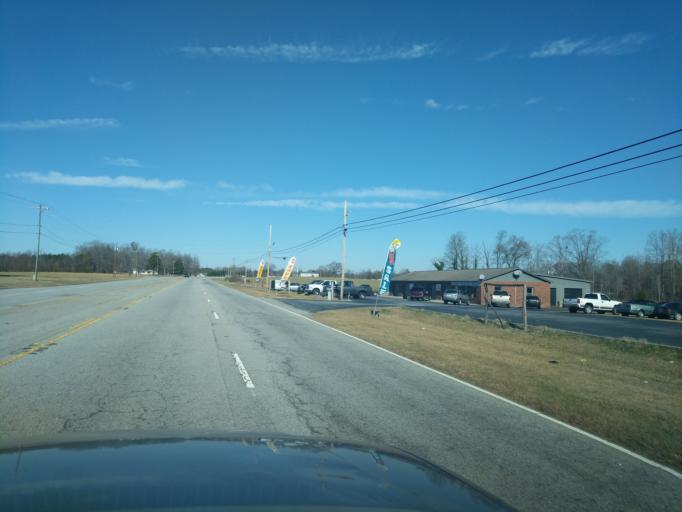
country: US
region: South Carolina
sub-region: Spartanburg County
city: Mayo
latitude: 35.1038
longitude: -81.8560
